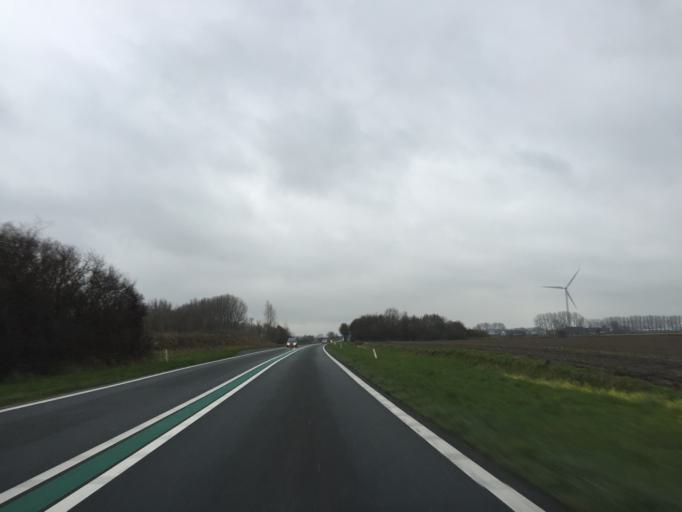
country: NL
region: Zeeland
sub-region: Gemeente Terneuzen
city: Axel
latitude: 51.2791
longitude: 3.8752
